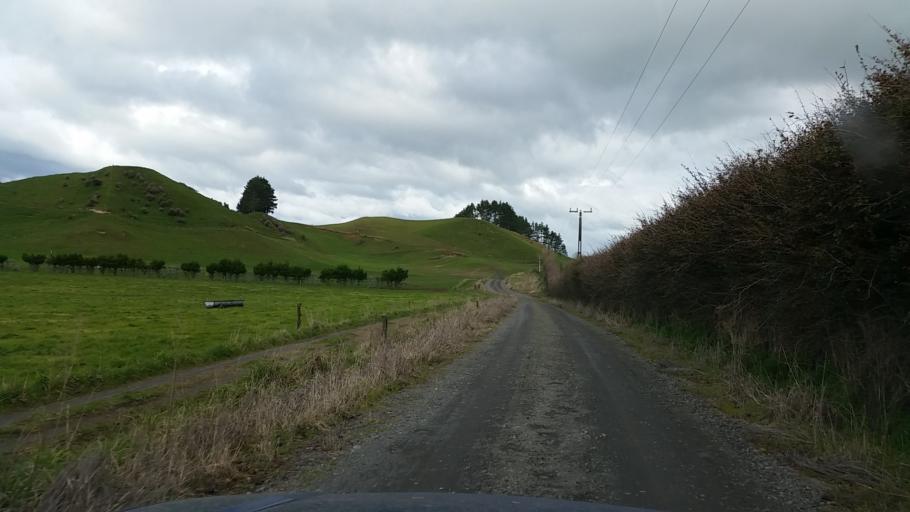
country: NZ
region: Taranaki
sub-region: South Taranaki District
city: Eltham
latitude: -39.3508
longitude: 174.3839
